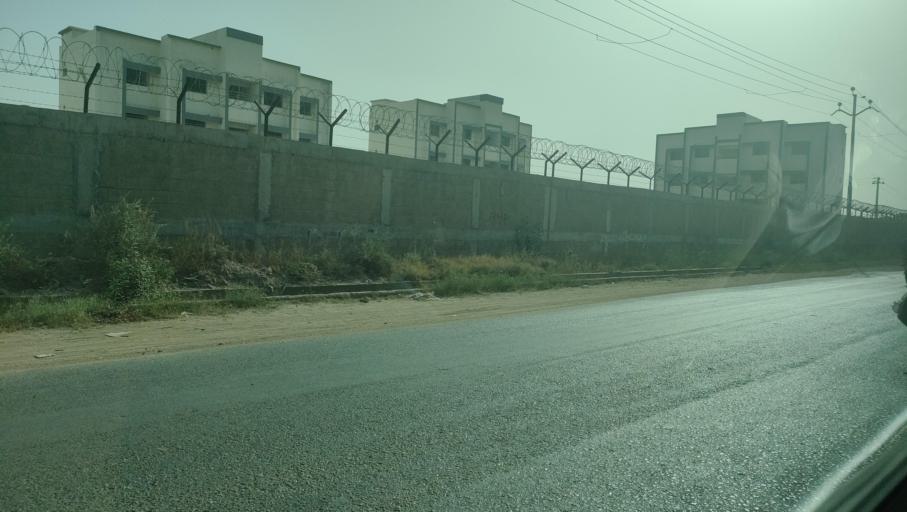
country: PK
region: Sindh
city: Malir Cantonment
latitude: 24.9235
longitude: 67.1817
